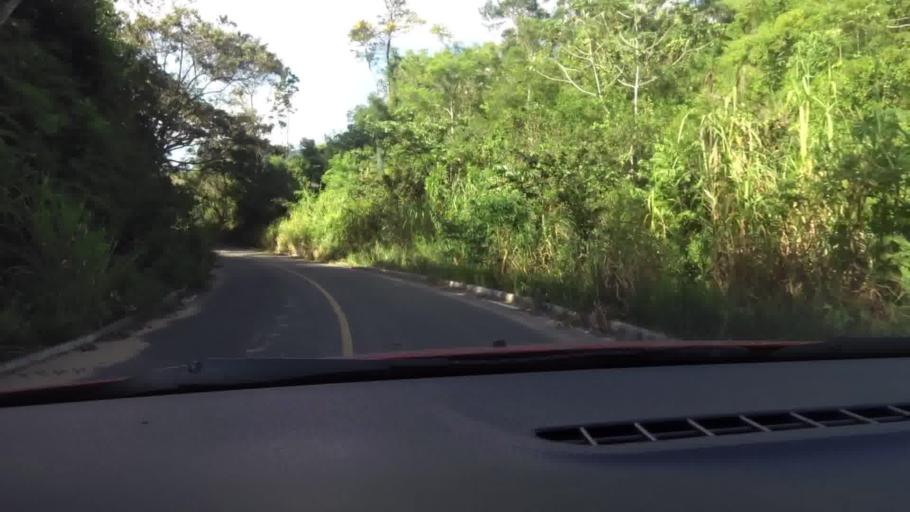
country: BR
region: Espirito Santo
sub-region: Guarapari
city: Guarapari
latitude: -20.5805
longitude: -40.5626
